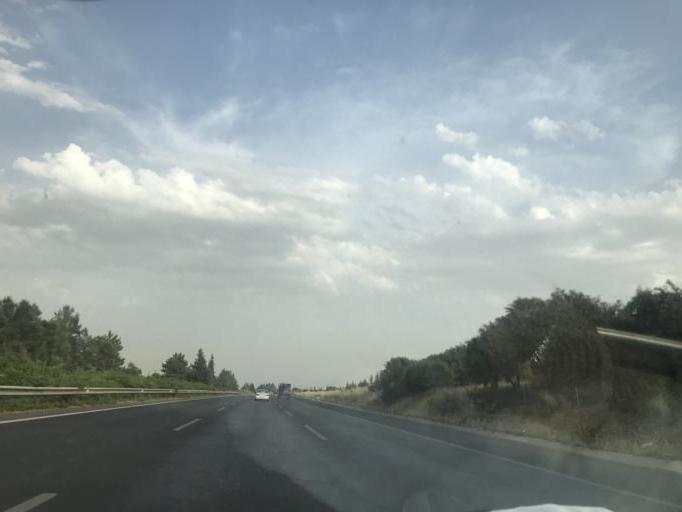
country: TR
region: Adana
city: Yakapinar
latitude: 37.0142
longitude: 35.5031
